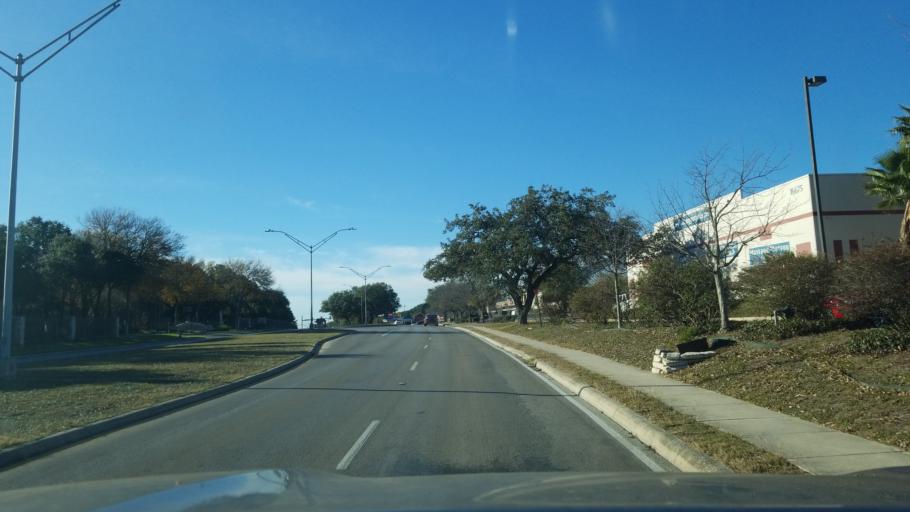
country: US
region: Texas
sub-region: Bexar County
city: Shavano Park
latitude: 29.5958
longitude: -98.5269
